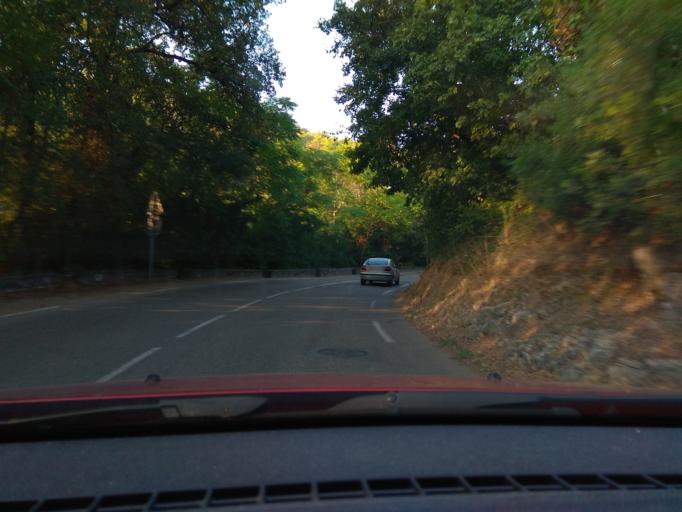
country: FR
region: Provence-Alpes-Cote d'Azur
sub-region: Departement des Alpes-Maritimes
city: La Colle-sur-Loup
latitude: 43.6806
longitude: 7.0830
